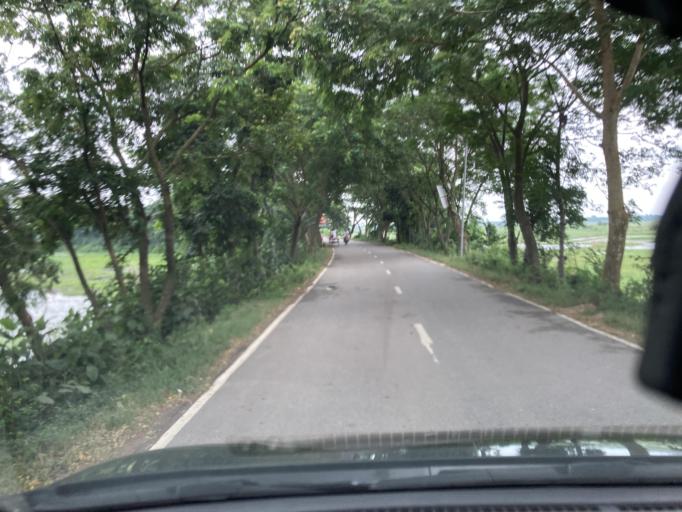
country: BD
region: Dhaka
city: Azimpur
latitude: 23.7744
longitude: 90.2063
